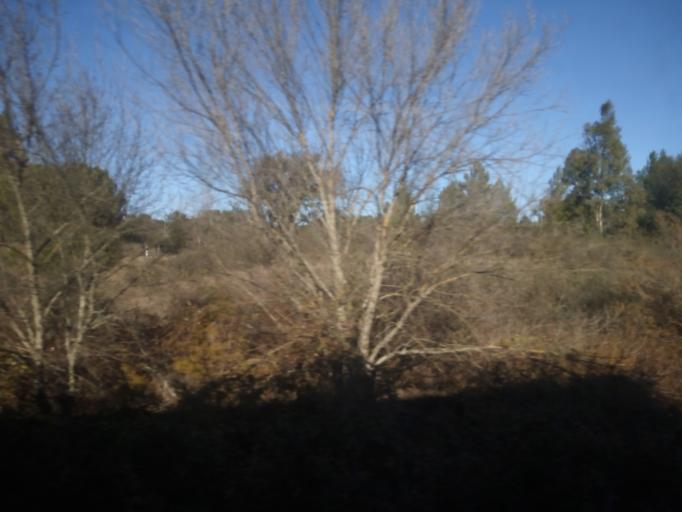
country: PT
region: Faro
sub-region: Silves
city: Sao Bartolomeu de Messines
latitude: 37.3348
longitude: -8.3452
